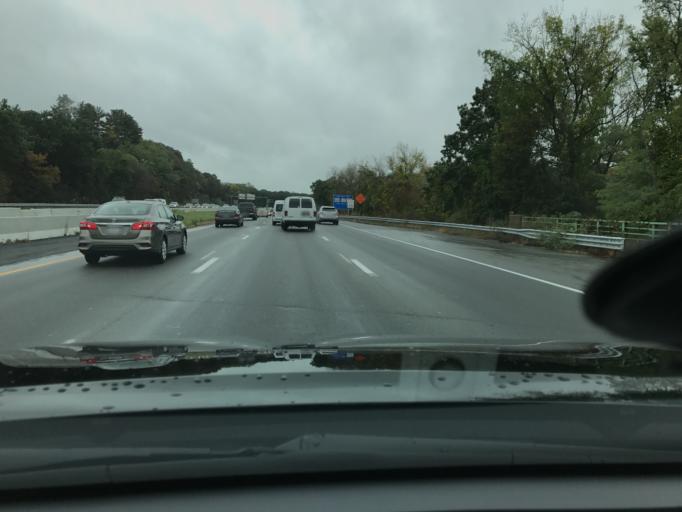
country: US
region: Massachusetts
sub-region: Middlesex County
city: Reading
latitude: 42.5109
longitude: -71.0924
